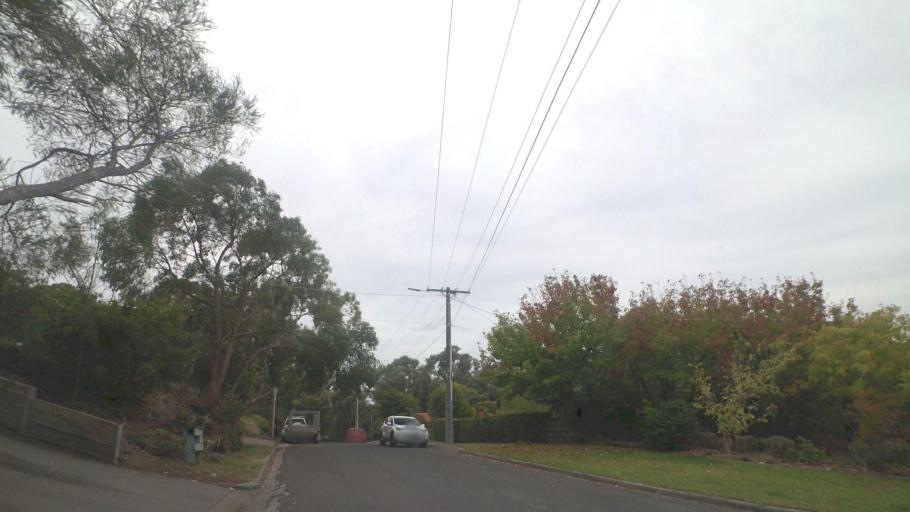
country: AU
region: Victoria
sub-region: Nillumbik
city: North Warrandyte
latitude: -37.7436
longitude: 145.2009
